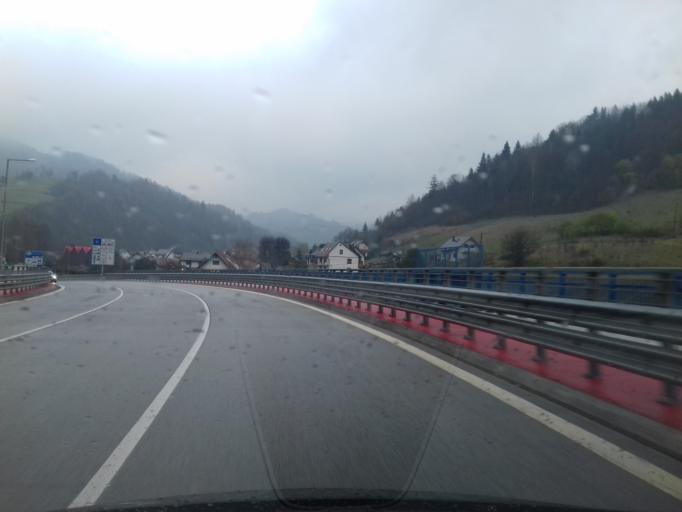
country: PL
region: Lesser Poland Voivodeship
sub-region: Powiat nowosadecki
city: Piwniczna-Zdroj
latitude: 49.4180
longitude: 20.7256
